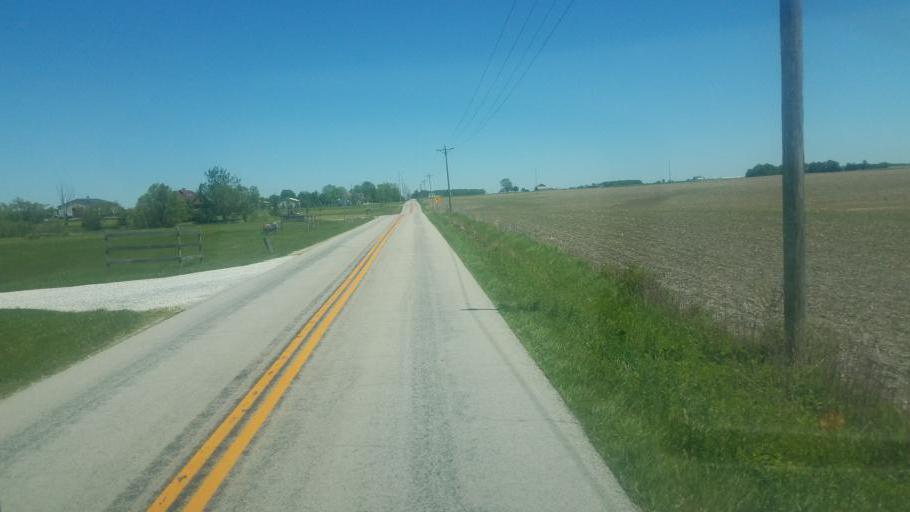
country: US
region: Ohio
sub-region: Miami County
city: Covington
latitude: 40.2270
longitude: -84.3432
